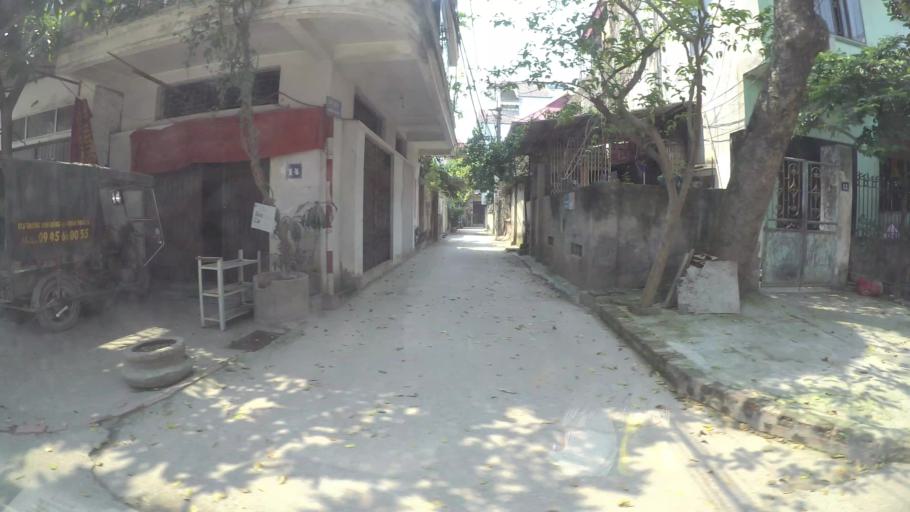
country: VN
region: Ha Noi
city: Ha Dong
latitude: 20.9860
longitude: 105.7640
